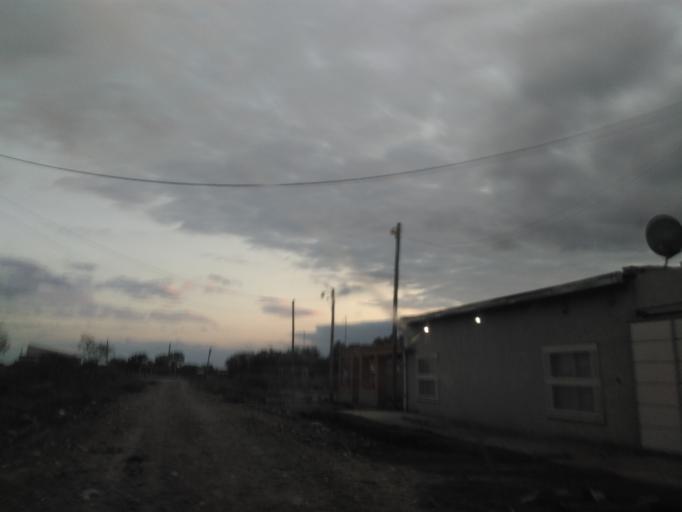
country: AR
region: Chaco
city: Resistencia
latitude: -27.4697
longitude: -59.0178
